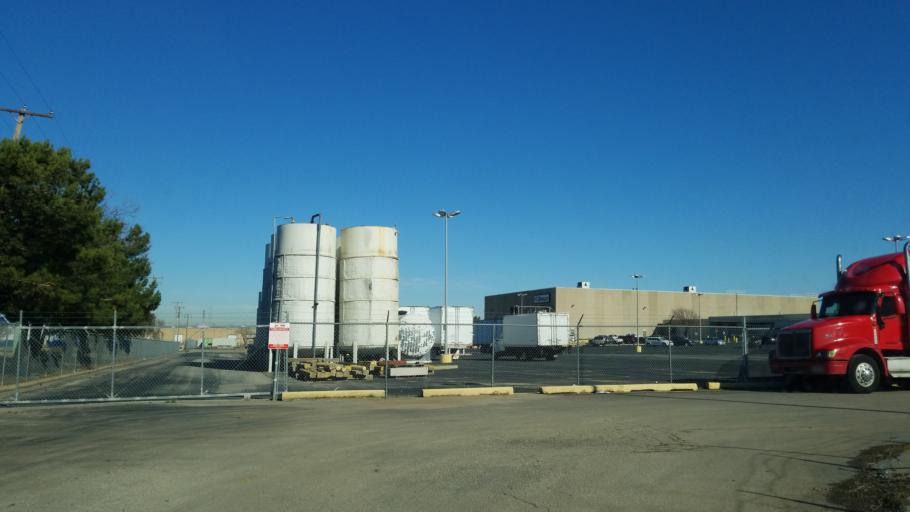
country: US
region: Texas
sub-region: Dallas County
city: Grand Prairie
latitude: 32.7415
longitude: -97.0508
